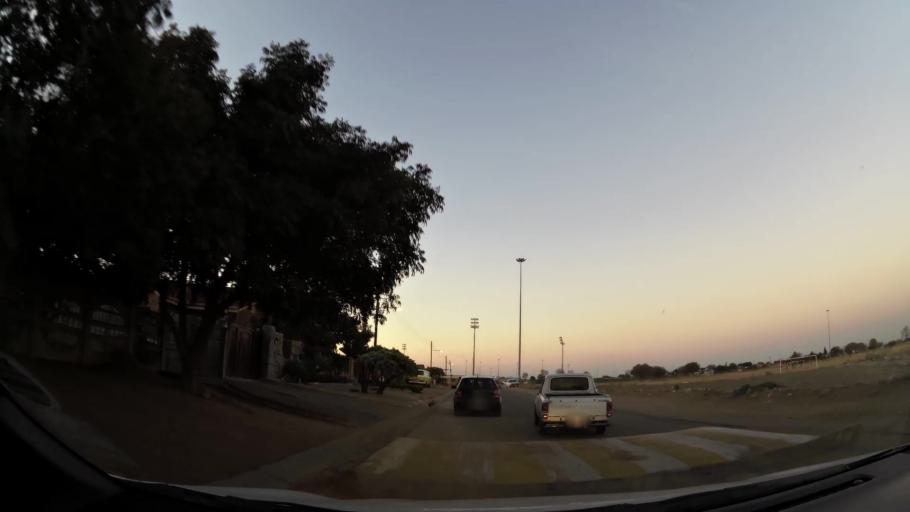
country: ZA
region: Limpopo
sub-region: Capricorn District Municipality
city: Polokwane
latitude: -23.8571
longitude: 29.3874
